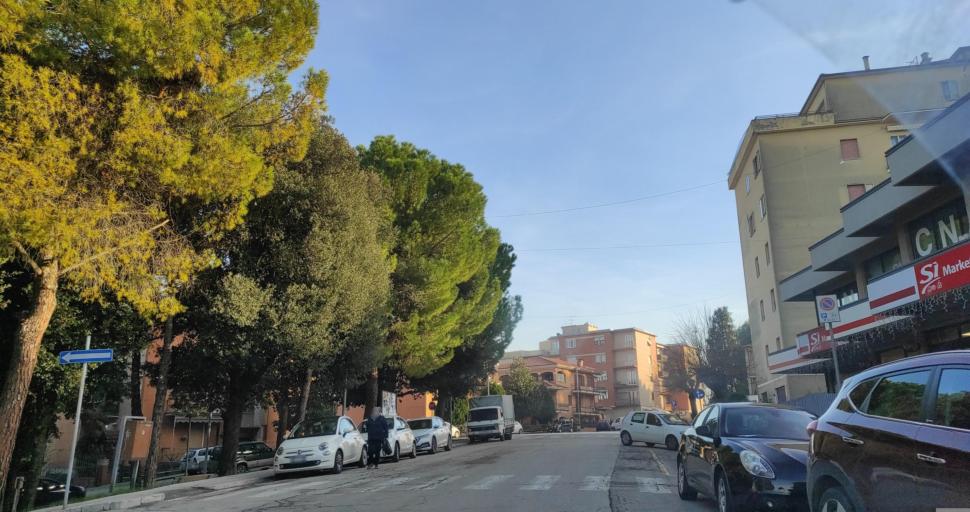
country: IT
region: The Marches
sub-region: Provincia di Macerata
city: Villa Potenza
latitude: 43.2993
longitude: 13.4292
